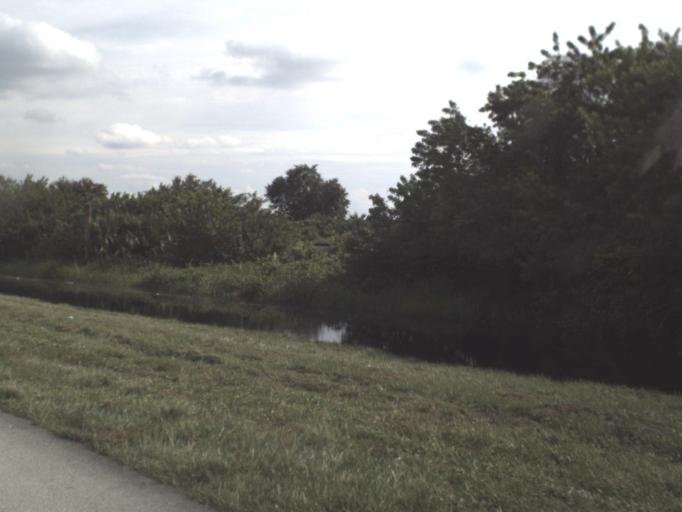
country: US
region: Florida
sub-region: Okeechobee County
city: Taylor Creek
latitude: 27.1889
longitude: -80.7225
